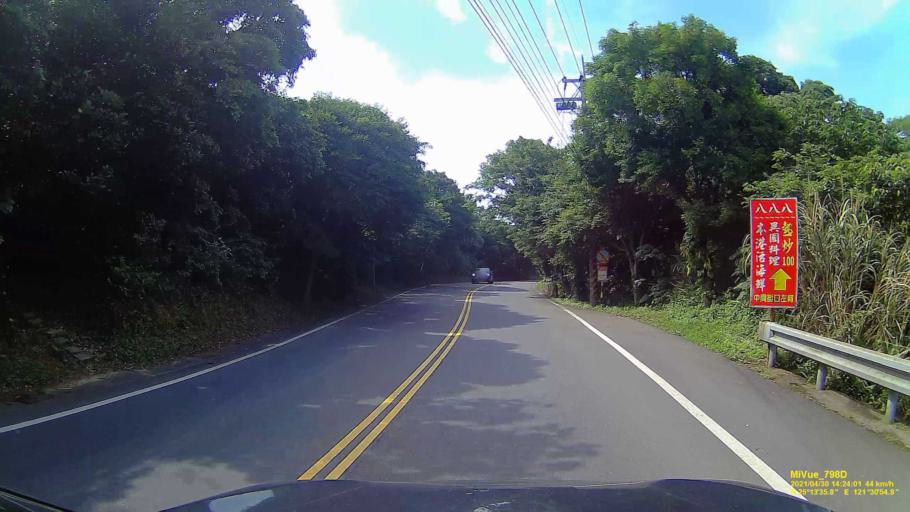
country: TW
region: Taipei
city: Taipei
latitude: 25.2268
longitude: 121.5151
